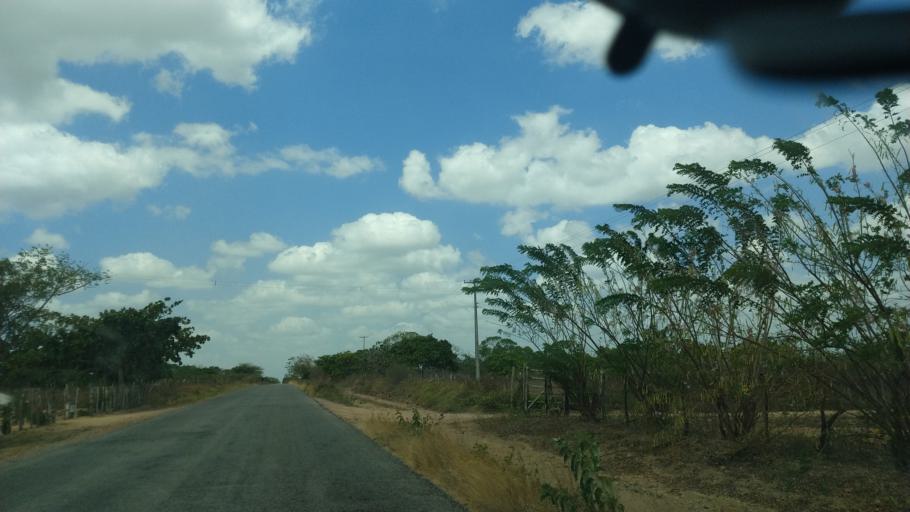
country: BR
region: Rio Grande do Norte
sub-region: Sao Paulo Do Potengi
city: Sao Paulo do Potengi
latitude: -5.9412
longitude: -35.8215
